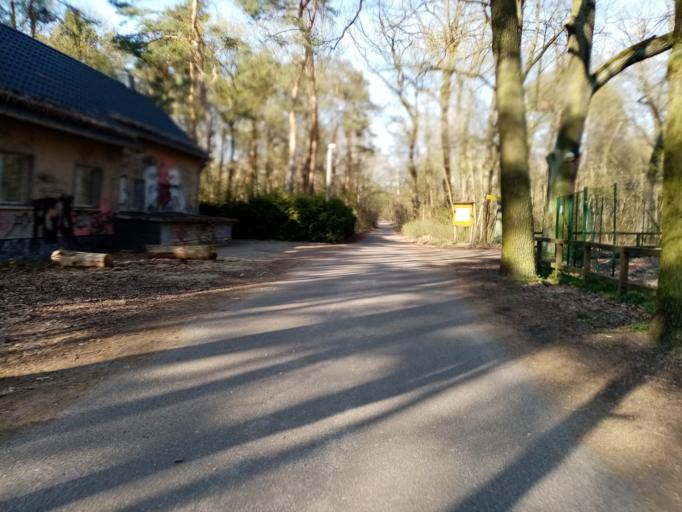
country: DE
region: Berlin
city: Oberschoneweide
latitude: 52.4644
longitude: 13.5411
